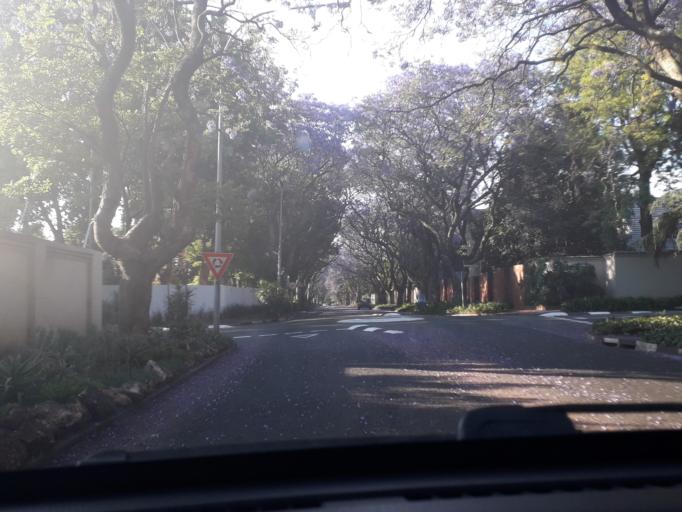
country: ZA
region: Gauteng
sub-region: City of Johannesburg Metropolitan Municipality
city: Johannesburg
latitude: -26.1564
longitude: 28.0392
